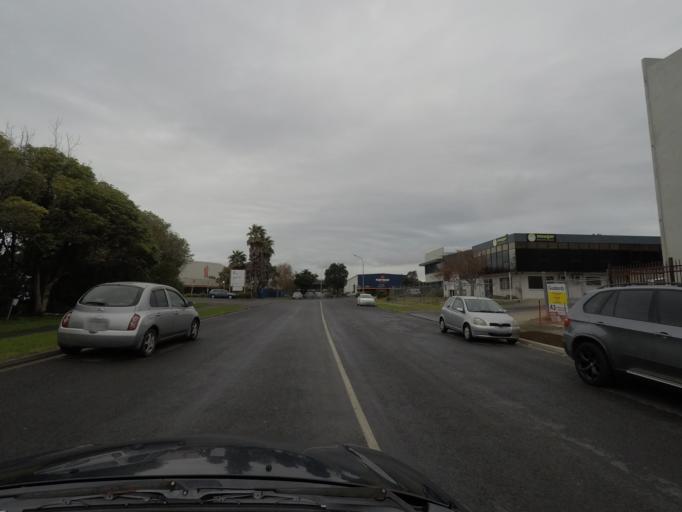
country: NZ
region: Auckland
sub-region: Auckland
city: Tamaki
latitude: -36.9296
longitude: 174.8856
